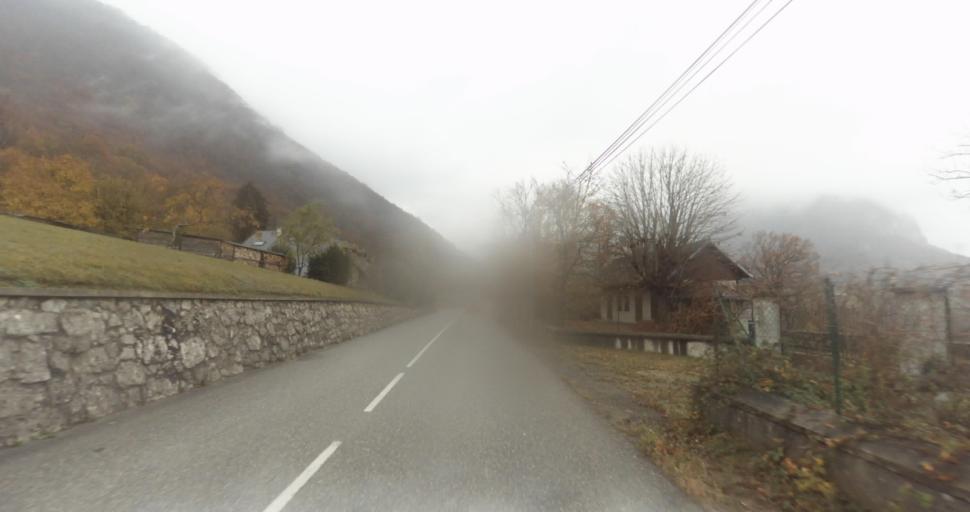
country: FR
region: Rhone-Alpes
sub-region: Departement de la Haute-Savoie
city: Gruffy
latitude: 45.7751
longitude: 6.0553
